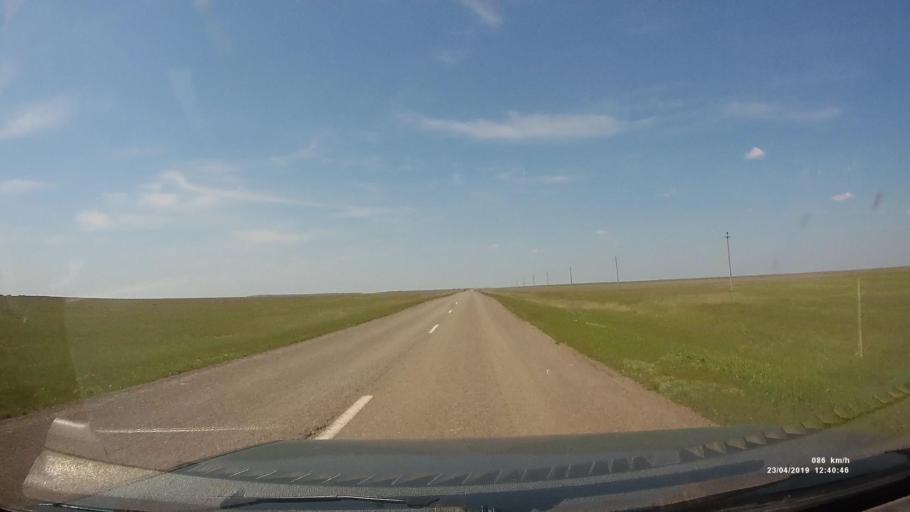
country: RU
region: Kalmykiya
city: Yashalta
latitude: 46.4428
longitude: 42.6915
